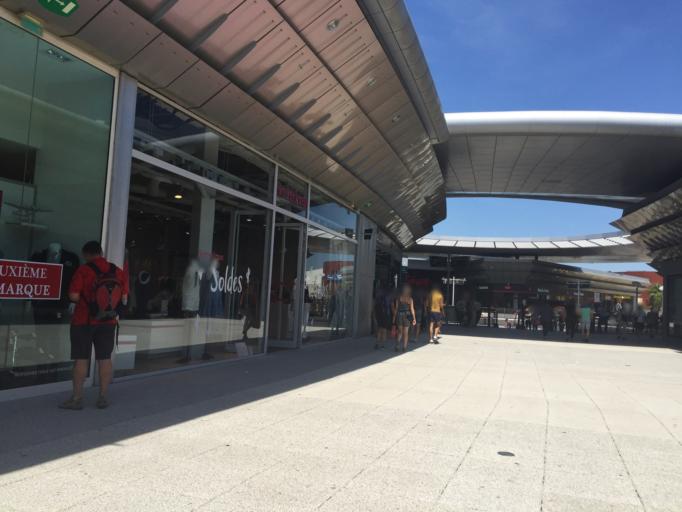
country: FR
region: Languedoc-Roussillon
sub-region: Departement de l'Herault
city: Castelnau-le-Lez
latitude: 43.6040
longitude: 3.9216
